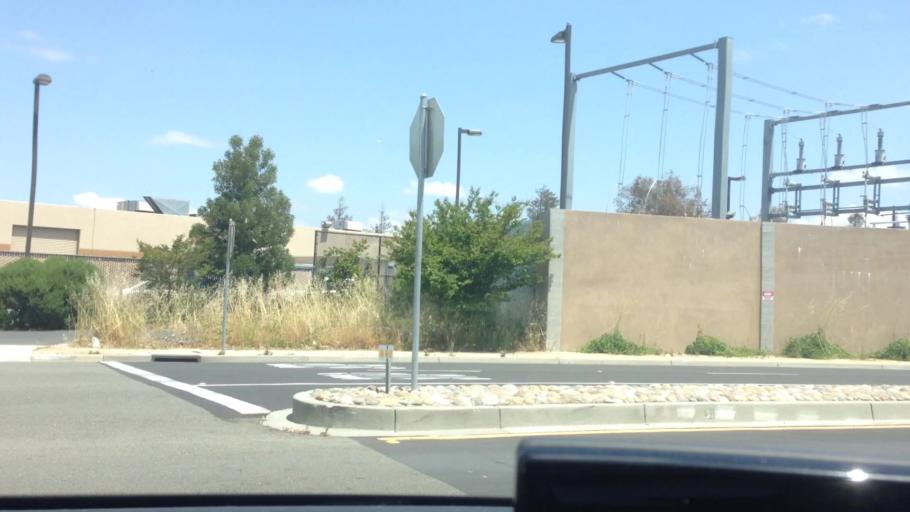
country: US
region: California
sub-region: Santa Clara County
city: Santa Clara
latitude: 37.3949
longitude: -121.9812
